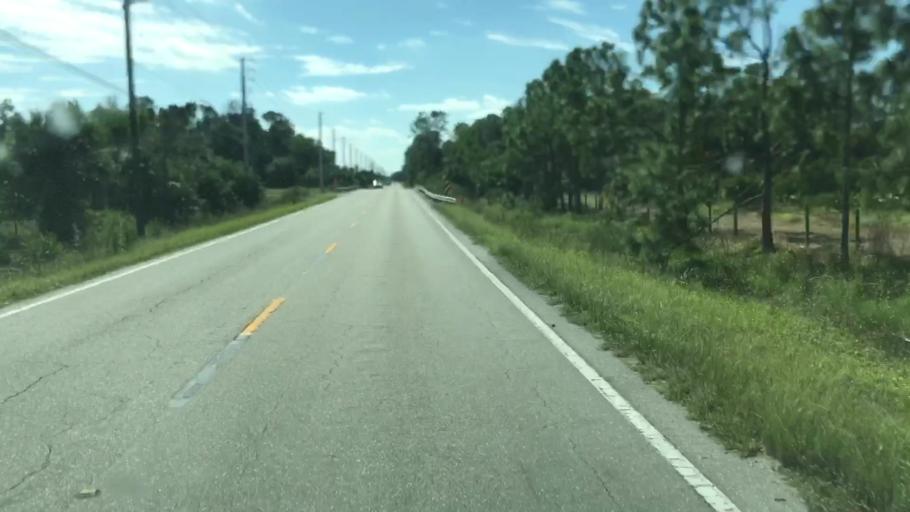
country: US
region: Florida
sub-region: Lee County
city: Bonita Springs
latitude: 26.3400
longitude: -81.7386
